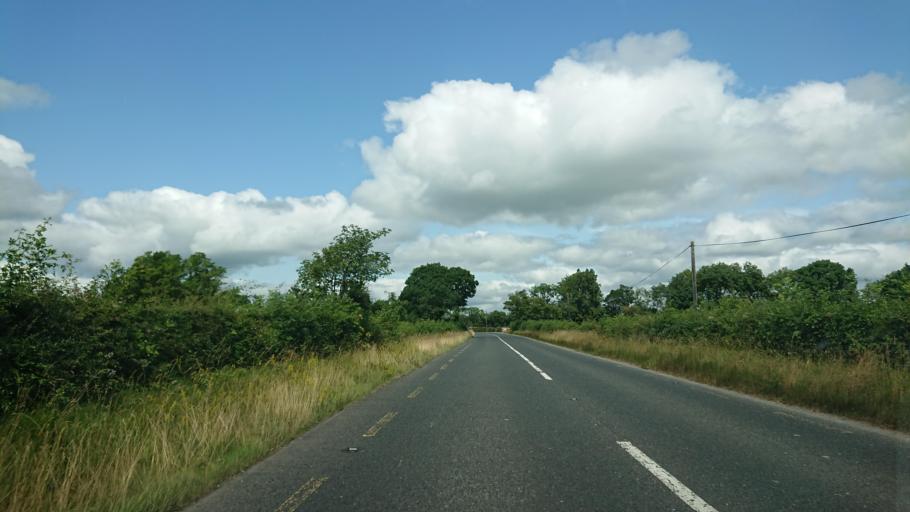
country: IE
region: Leinster
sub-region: Kildare
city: Kilcock
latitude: 53.3674
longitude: -6.6994
